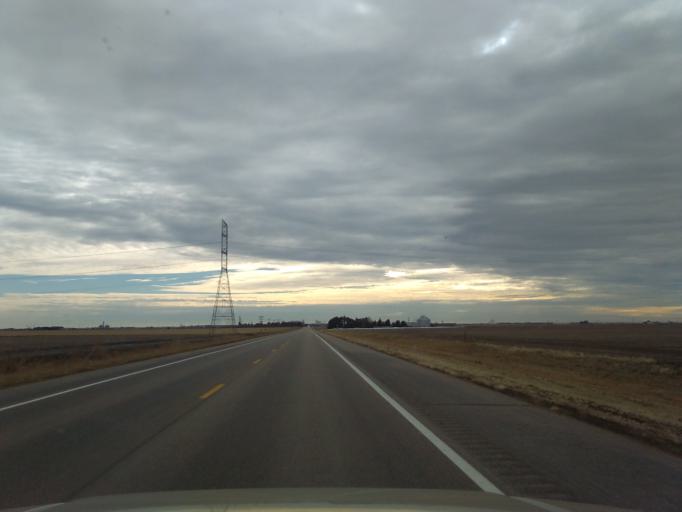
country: US
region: Nebraska
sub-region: Kearney County
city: Minden
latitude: 40.5492
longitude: -98.9519
